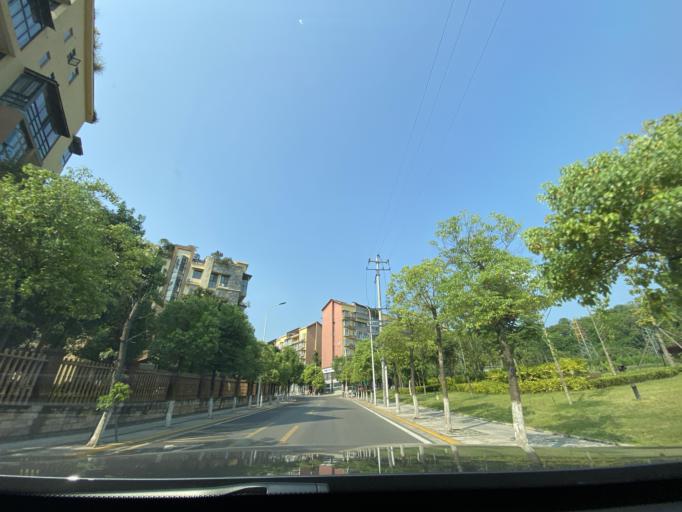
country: CN
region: Sichuan
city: Jiancheng
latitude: 30.4168
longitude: 104.5436
